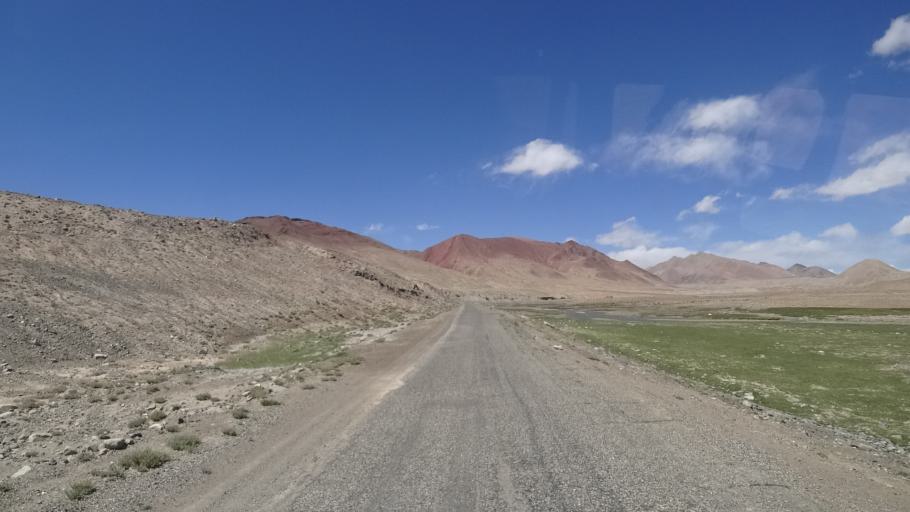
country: TJ
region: Gorno-Badakhshan
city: Murghob
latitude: 38.4932
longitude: 73.8458
